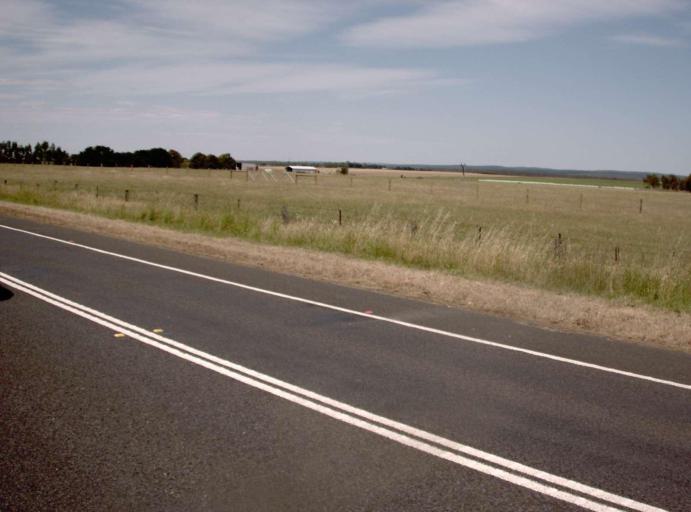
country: AU
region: Victoria
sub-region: Wellington
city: Heyfield
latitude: -38.1261
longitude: 146.8391
